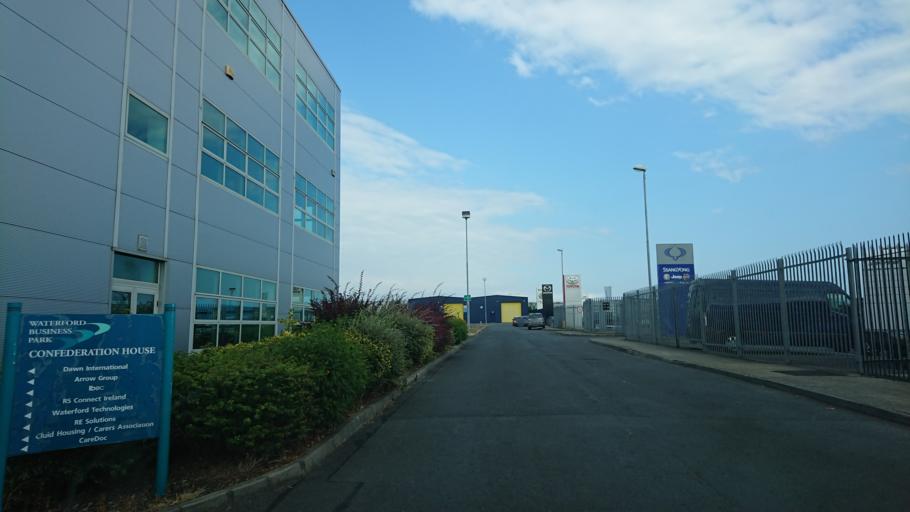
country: IE
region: Munster
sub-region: Waterford
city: Waterford
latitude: 52.2441
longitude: -7.1588
